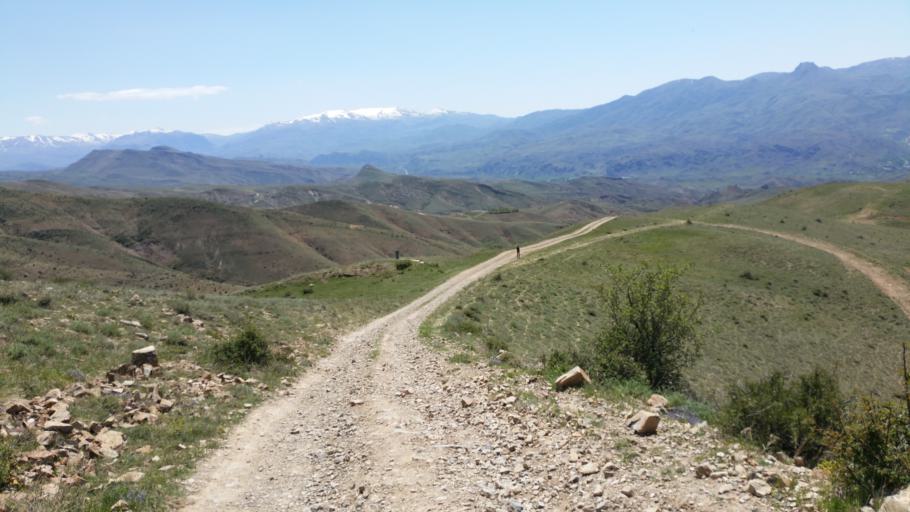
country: AM
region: Vayots' Dzori Marz
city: Vernashen
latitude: 39.8030
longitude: 45.3600
